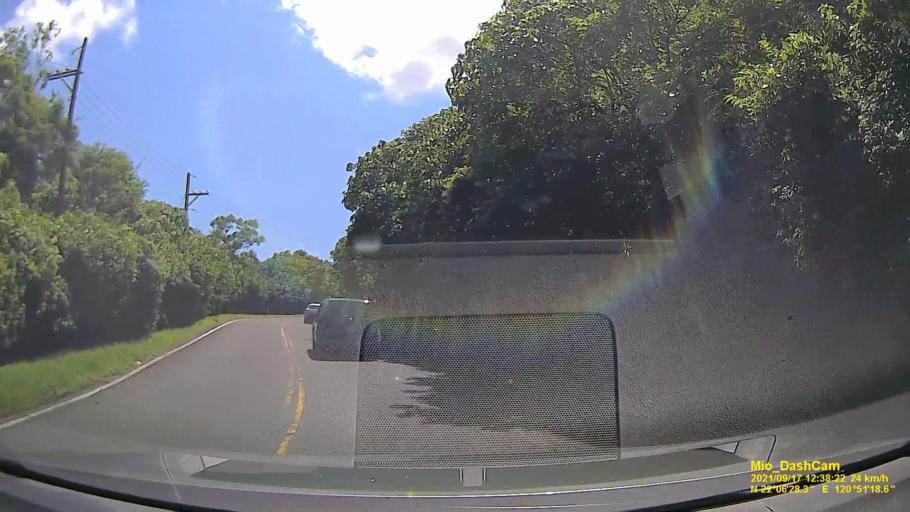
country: TW
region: Taiwan
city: Hengchun
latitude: 22.1079
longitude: 120.8552
